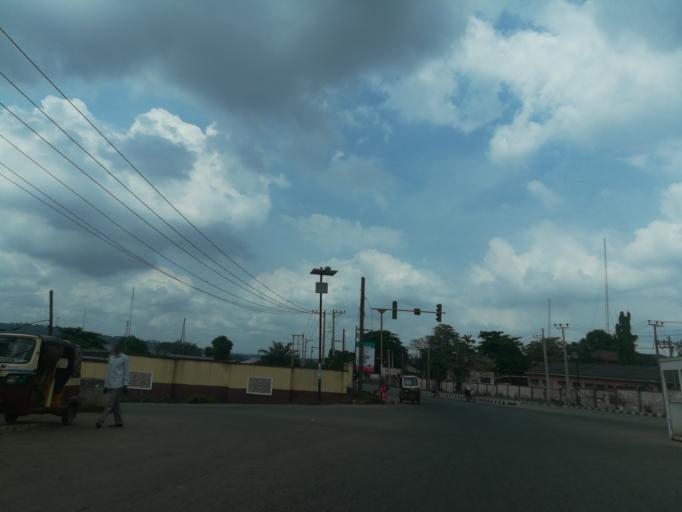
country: NG
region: Oyo
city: Ibadan
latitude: 7.3972
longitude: 3.9175
